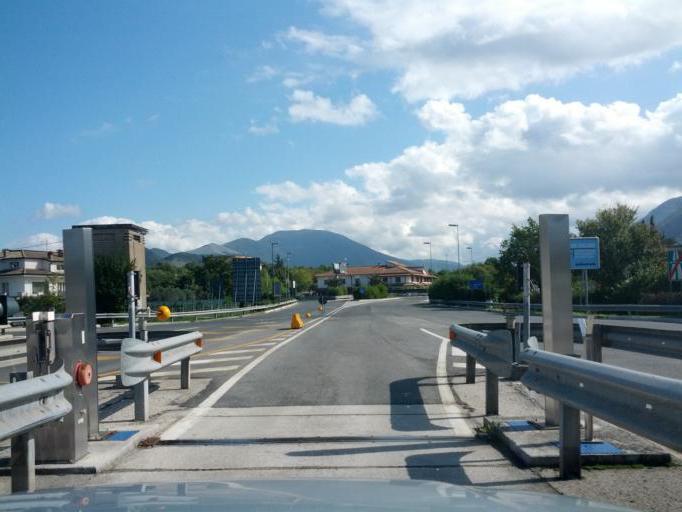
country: IT
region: Campania
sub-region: Provincia di Caserta
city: Bivio Mortola
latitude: 41.4333
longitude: 13.9011
